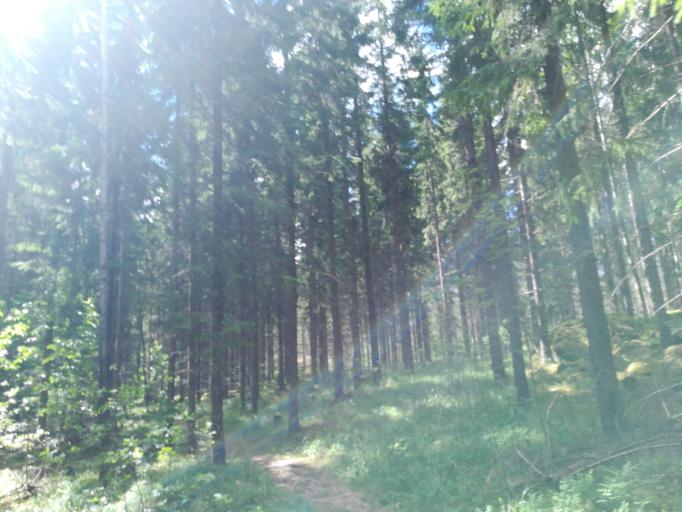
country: FI
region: Southern Savonia
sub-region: Mikkeli
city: Maentyharju
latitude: 61.3650
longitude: 26.9338
